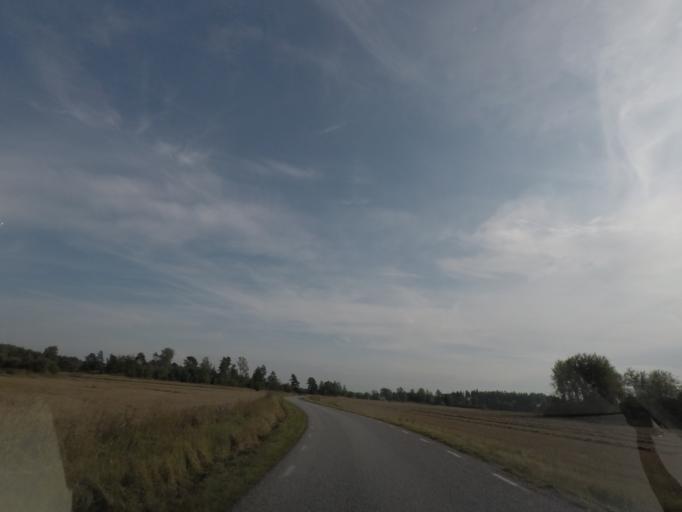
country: SE
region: Vaestmanland
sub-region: Kungsors Kommun
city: Kungsoer
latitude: 59.5253
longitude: 16.1434
